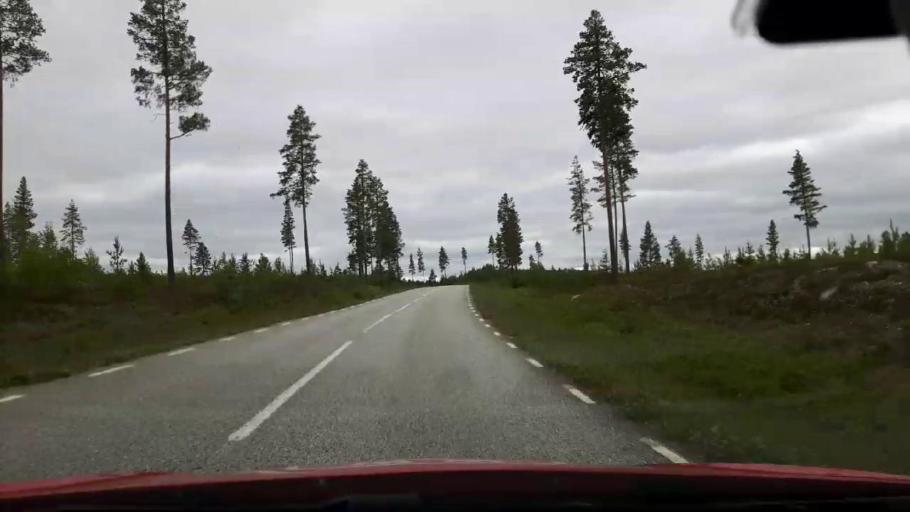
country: SE
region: Jaemtland
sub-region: Stroemsunds Kommun
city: Stroemsund
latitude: 63.3644
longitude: 15.7135
